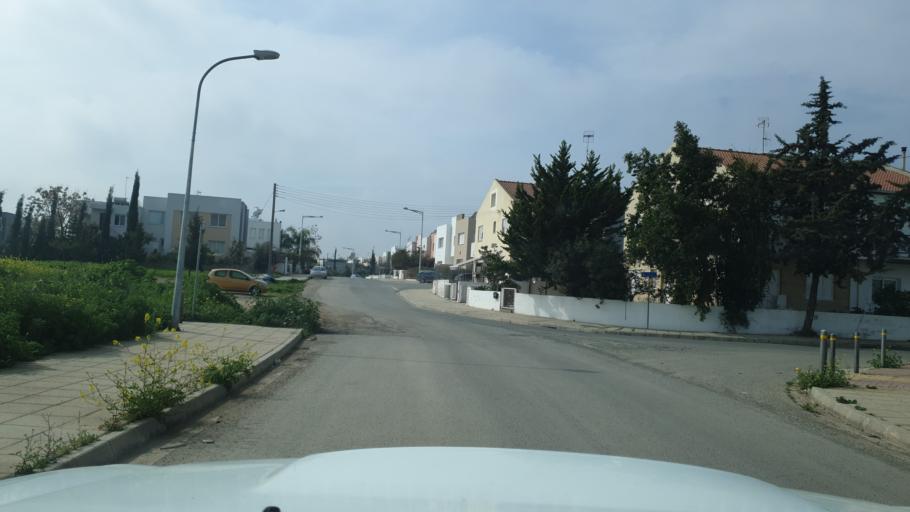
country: CY
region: Lefkosia
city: Nicosia
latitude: 35.1227
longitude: 33.3510
